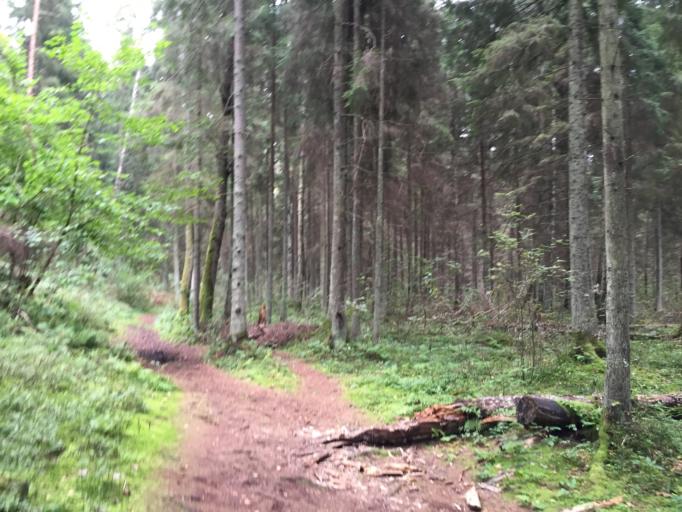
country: LV
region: Ogre
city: Ogre
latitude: 56.8321
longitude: 24.5771
